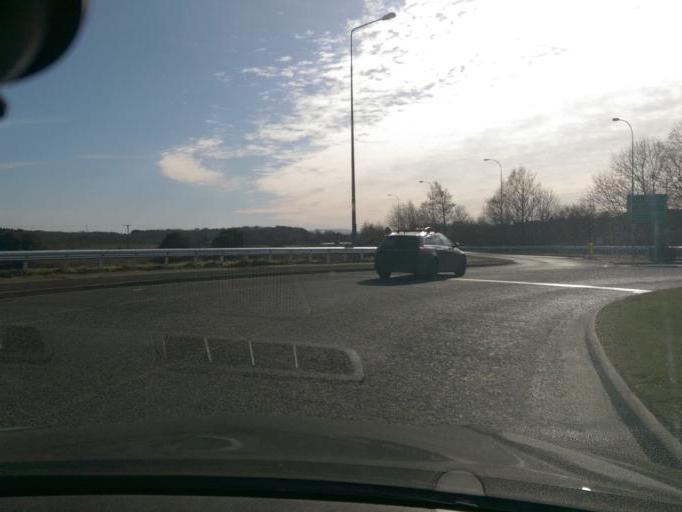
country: IE
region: Connaught
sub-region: County Galway
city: Oranmore
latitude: 53.2716
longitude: -8.9175
